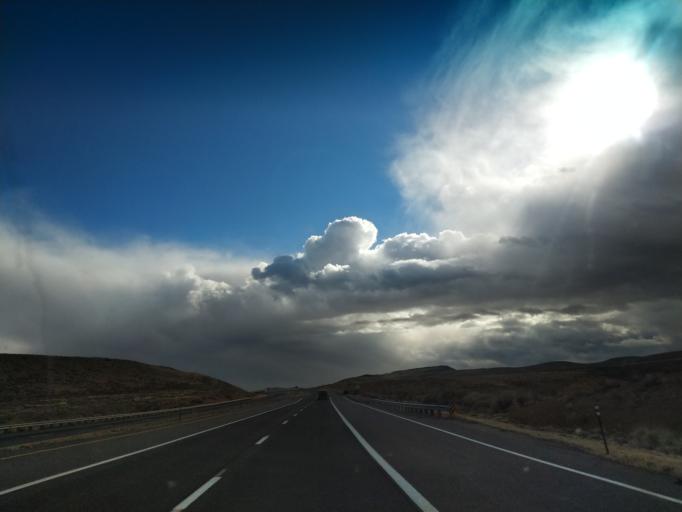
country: US
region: Colorado
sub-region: Delta County
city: Delta
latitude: 38.7738
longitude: -108.2305
